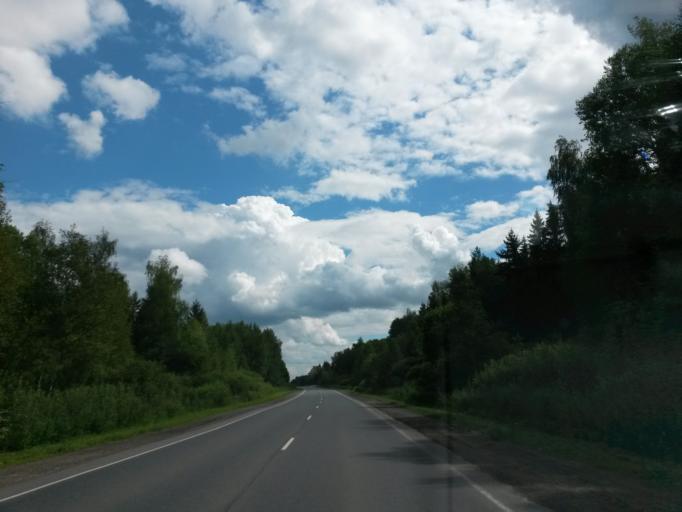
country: RU
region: Ivanovo
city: Pistsovo
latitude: 57.1254
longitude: 40.6111
